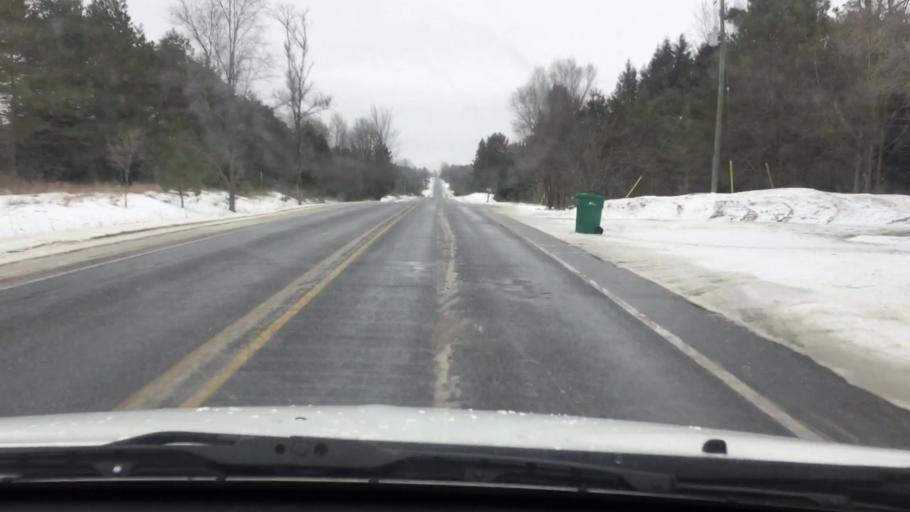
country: US
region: Michigan
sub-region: Wexford County
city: Cadillac
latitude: 44.0919
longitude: -85.4442
